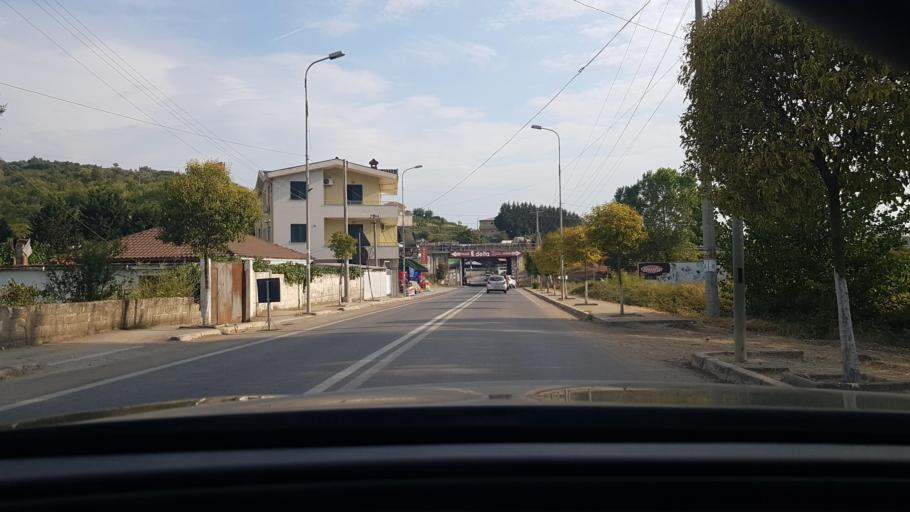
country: AL
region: Durres
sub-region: Rrethi i Durresit
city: Maminas
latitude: 41.3727
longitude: 19.6058
